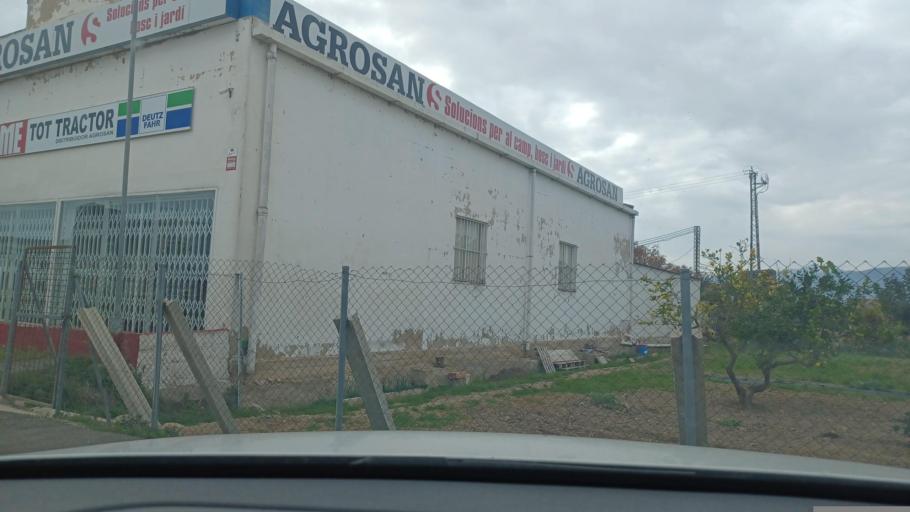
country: ES
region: Catalonia
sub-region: Provincia de Tarragona
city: Amposta
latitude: 40.7073
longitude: 0.5912
